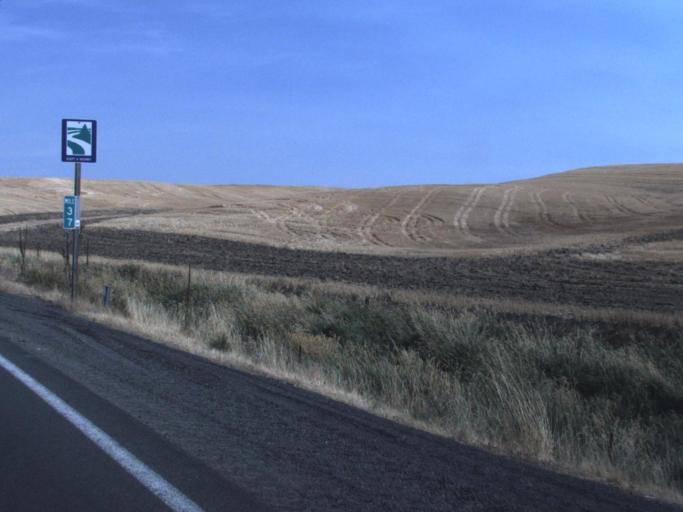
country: US
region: Washington
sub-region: Whitman County
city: Colfax
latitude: 47.1363
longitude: -117.2407
